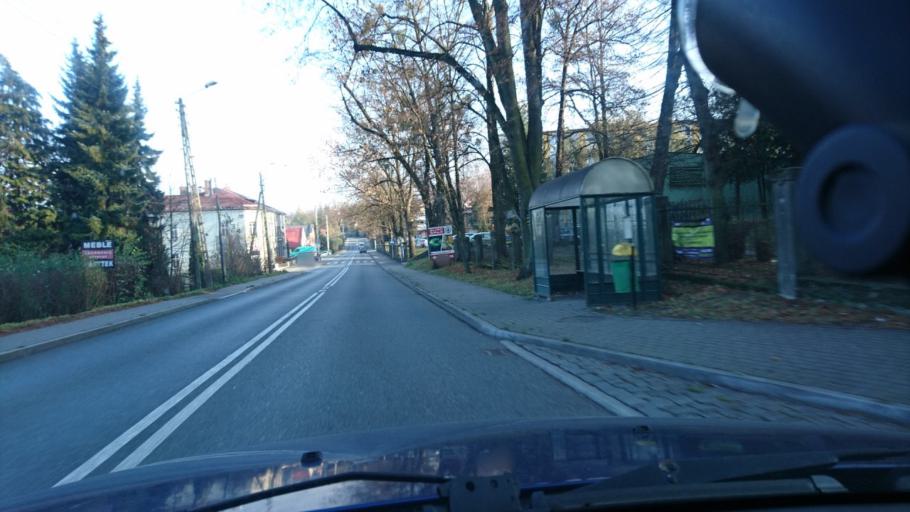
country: PL
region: Silesian Voivodeship
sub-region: Powiat cieszynski
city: Cieszyn
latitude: 49.7499
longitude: 18.6489
